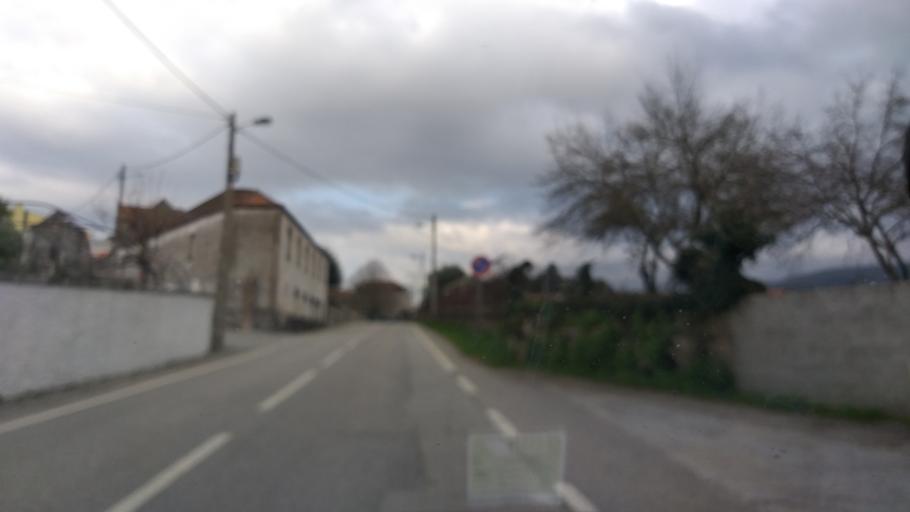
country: PT
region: Guarda
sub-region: Seia
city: Seia
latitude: 40.4933
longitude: -7.6279
